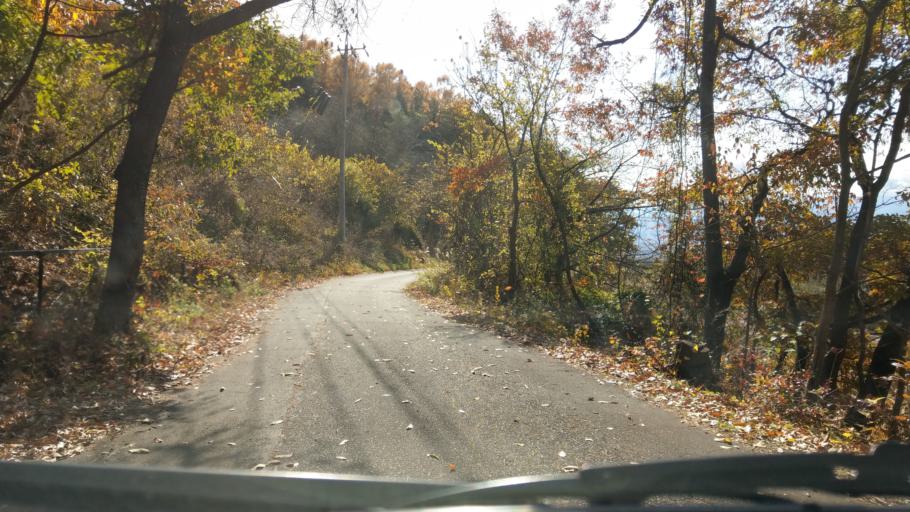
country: JP
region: Nagano
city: Komoro
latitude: 36.3439
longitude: 138.4463
